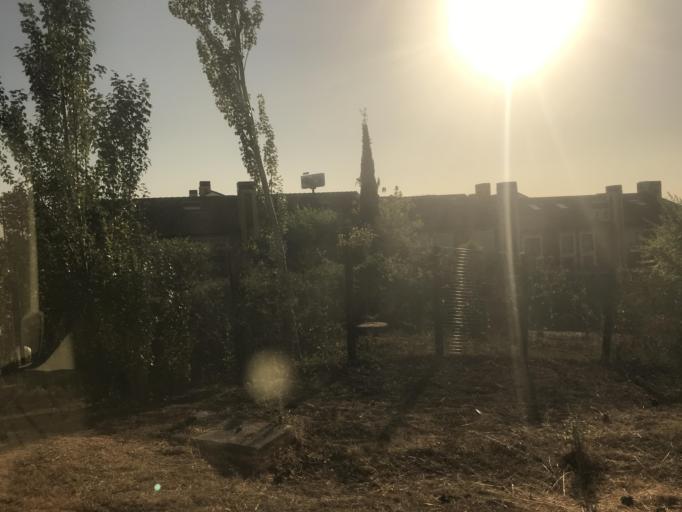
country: ES
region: Madrid
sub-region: Provincia de Madrid
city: Majadahonda
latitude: 40.4777
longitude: -3.8502
